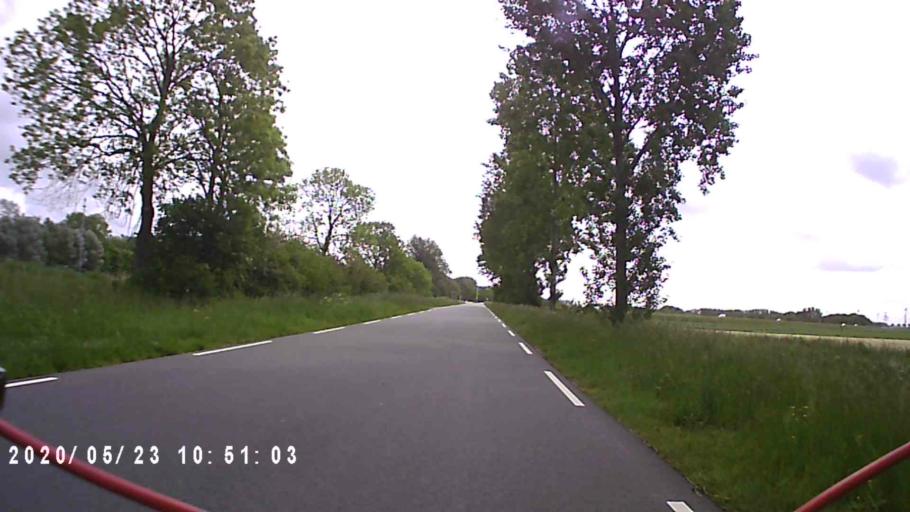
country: NL
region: Groningen
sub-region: Gemeente Delfzijl
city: Delfzijl
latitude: 53.3145
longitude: 6.9383
